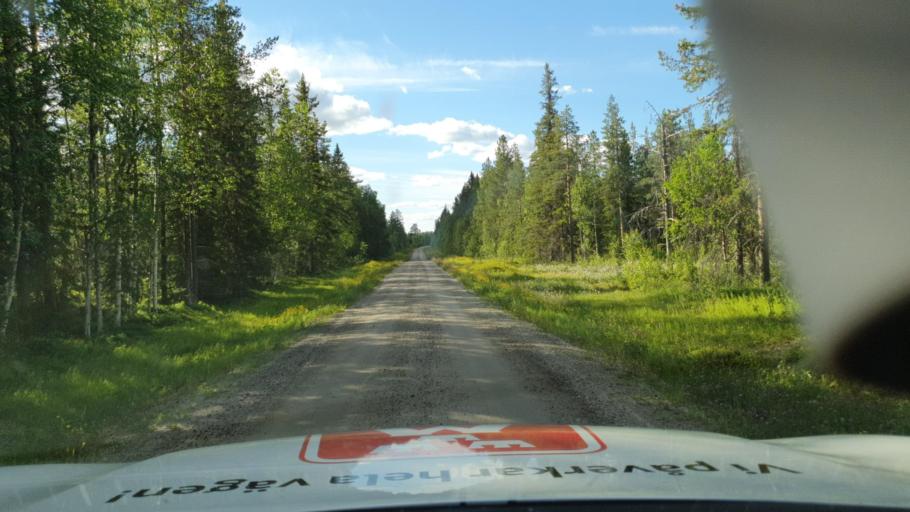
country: SE
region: Vaesterbotten
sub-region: Lycksele Kommun
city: Lycksele
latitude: 64.4695
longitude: 18.2918
